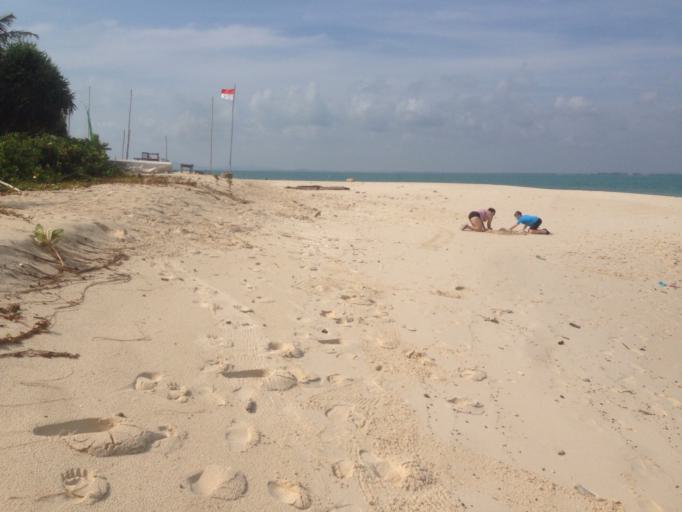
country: ID
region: Riau Islands
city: Kijang
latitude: 1.0523
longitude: 104.7071
